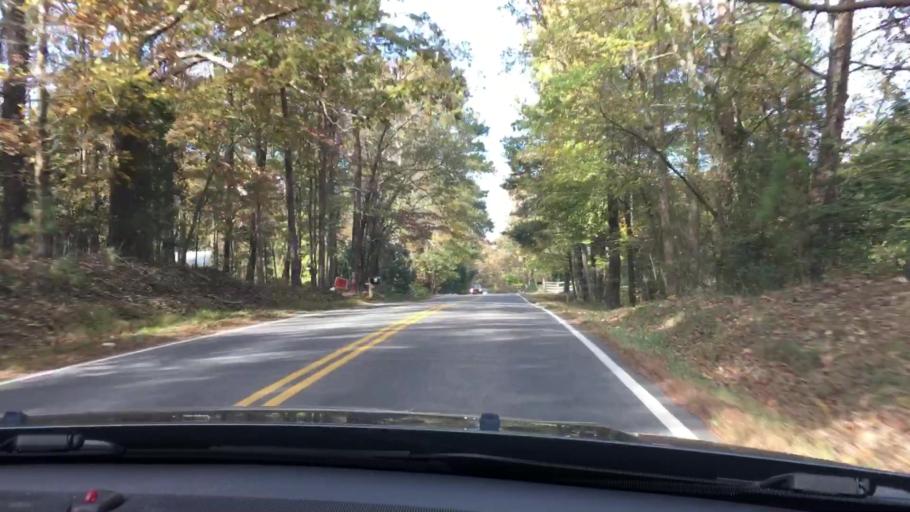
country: US
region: Virginia
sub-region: King William County
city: West Point
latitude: 37.4921
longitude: -76.8144
